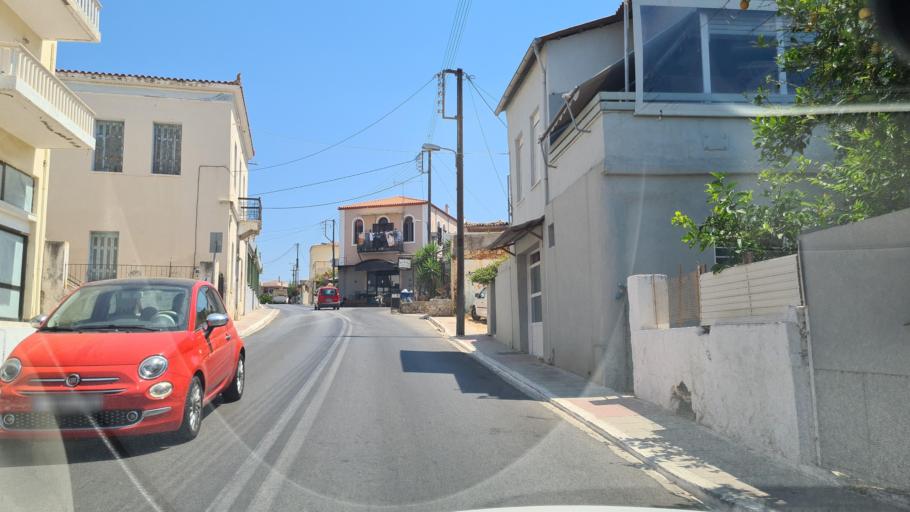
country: GR
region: Crete
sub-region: Nomos Chanias
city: Chania
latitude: 35.5186
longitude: 24.0404
